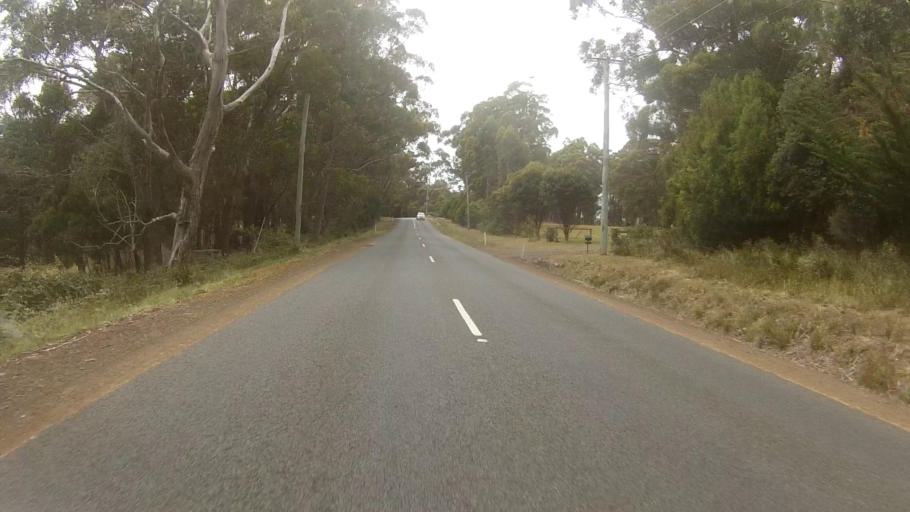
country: AU
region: Tasmania
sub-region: Kingborough
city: Margate
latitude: -42.9931
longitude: 147.2060
